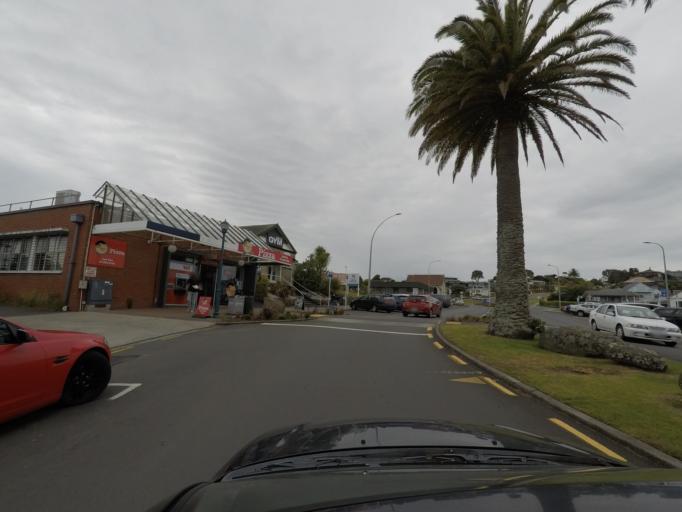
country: NZ
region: Waikato
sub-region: Waikato District
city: Raglan
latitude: -37.8001
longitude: 174.8702
